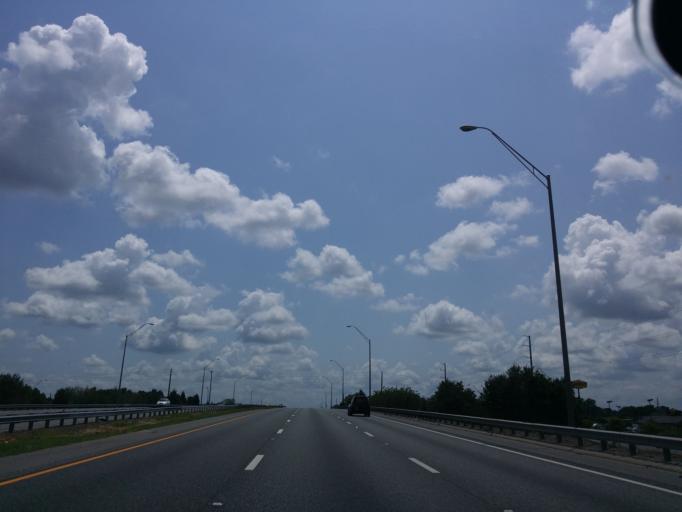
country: US
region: Florida
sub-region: Marion County
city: Ocala
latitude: 29.1888
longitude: -82.1848
